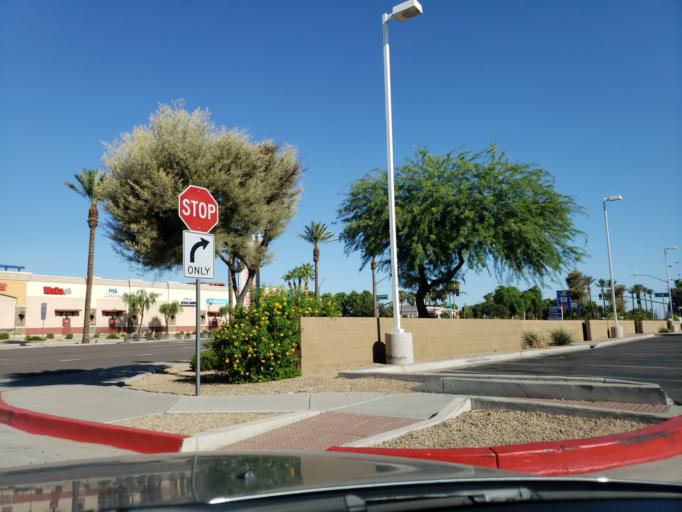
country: US
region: Arizona
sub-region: Maricopa County
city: Tolleson
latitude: 33.4637
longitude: -112.2722
